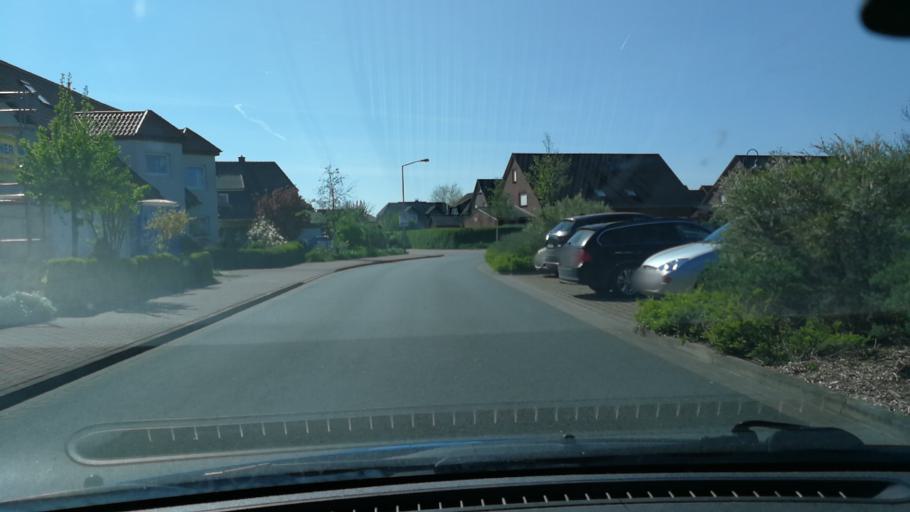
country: DE
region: Lower Saxony
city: Lehrte
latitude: 52.3710
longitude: 9.9161
